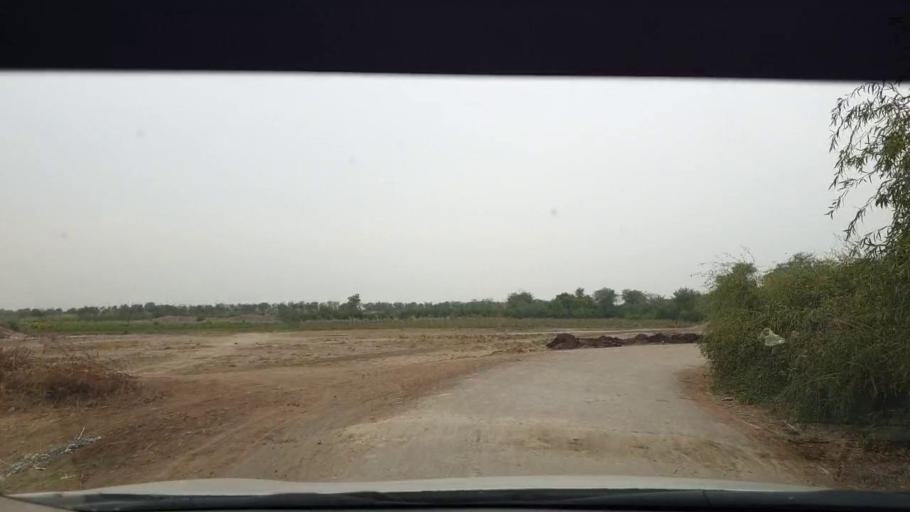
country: PK
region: Sindh
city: Berani
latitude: 25.8742
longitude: 68.7946
